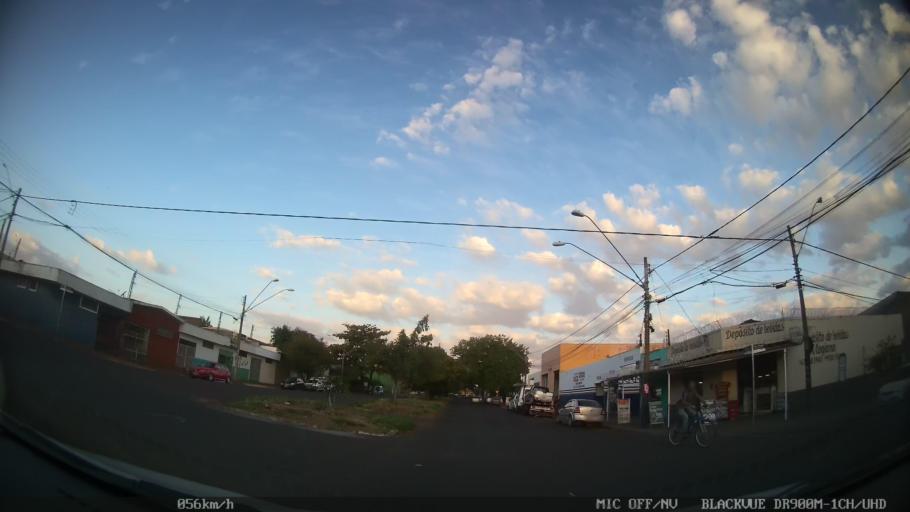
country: BR
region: Sao Paulo
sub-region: Ribeirao Preto
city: Ribeirao Preto
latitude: -21.1451
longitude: -47.7937
